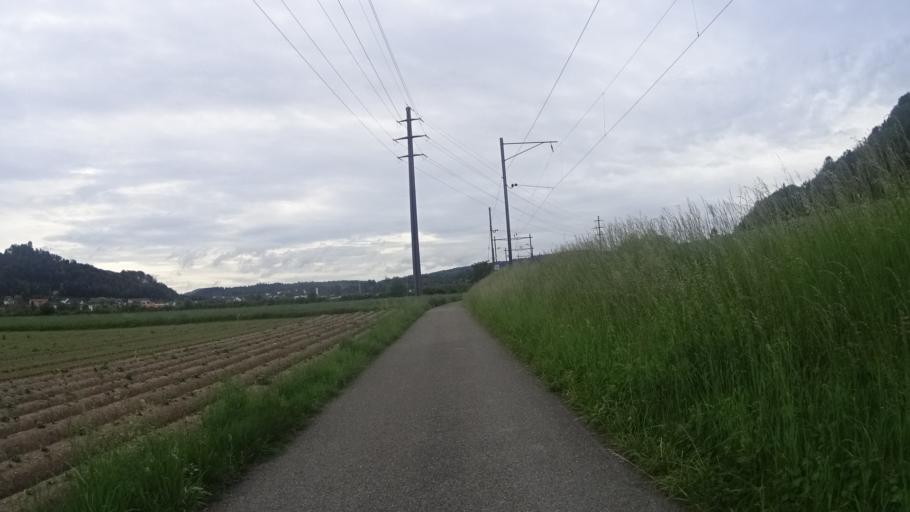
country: DE
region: Baden-Wuerttemberg
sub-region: Freiburg Region
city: Waldshut-Tiengen
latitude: 47.6100
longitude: 8.2166
